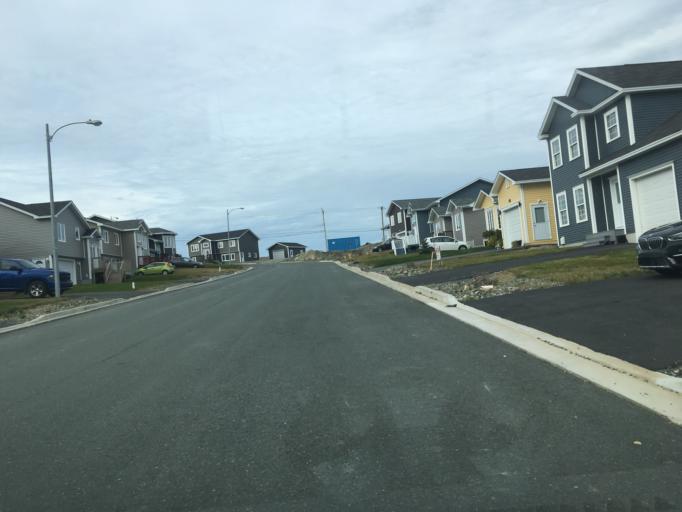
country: CA
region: Newfoundland and Labrador
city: Mount Pearl
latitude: 47.5514
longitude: -52.7840
